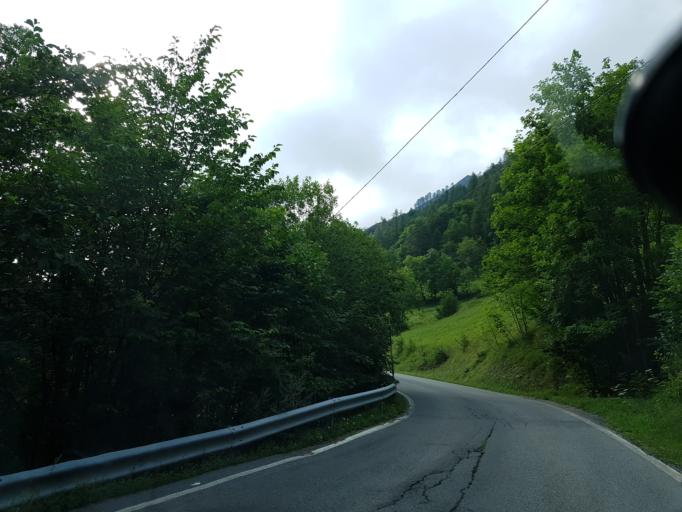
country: IT
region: Piedmont
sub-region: Provincia di Cuneo
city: Casteldelfino
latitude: 44.5858
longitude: 7.0525
